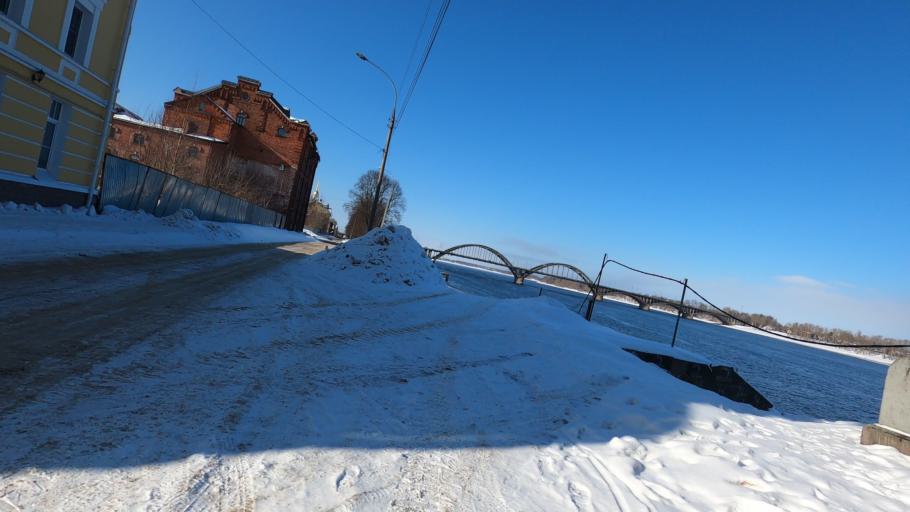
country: RU
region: Jaroslavl
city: Rybinsk
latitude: 58.0464
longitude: 38.8701
